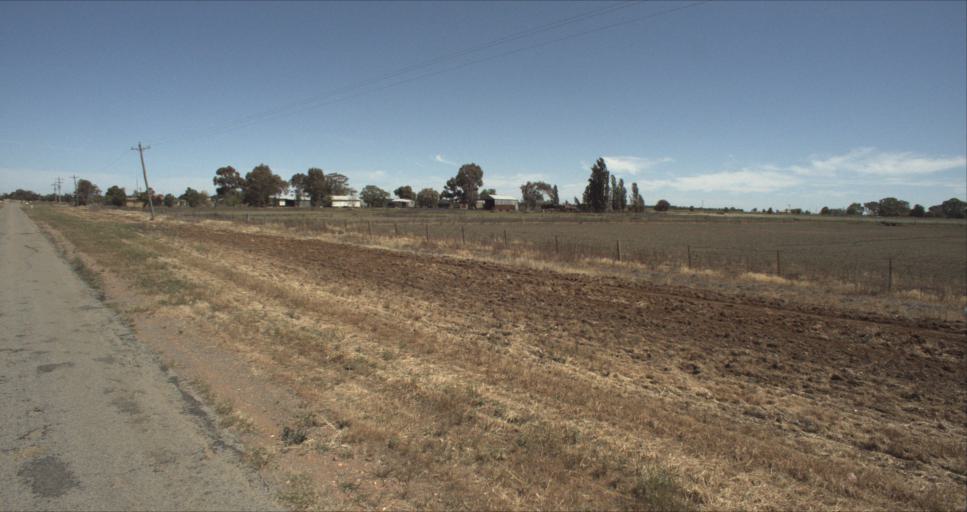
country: AU
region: New South Wales
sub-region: Leeton
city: Leeton
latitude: -34.5087
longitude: 146.3447
